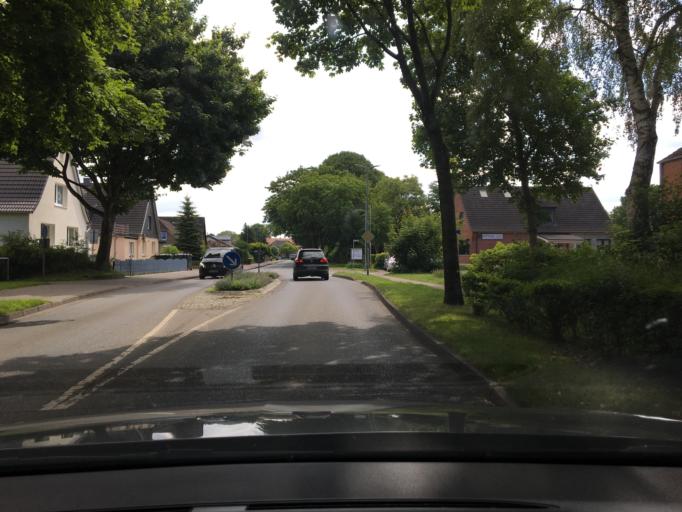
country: DE
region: Schleswig-Holstein
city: Kropp
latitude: 54.4141
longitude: 9.5043
